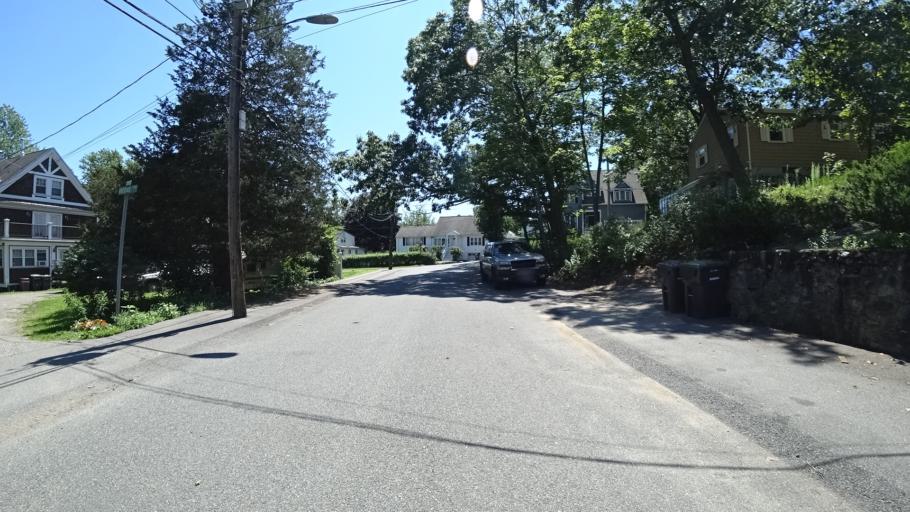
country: US
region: Massachusetts
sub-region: Norfolk County
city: Dedham
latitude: 42.2604
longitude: -71.1756
